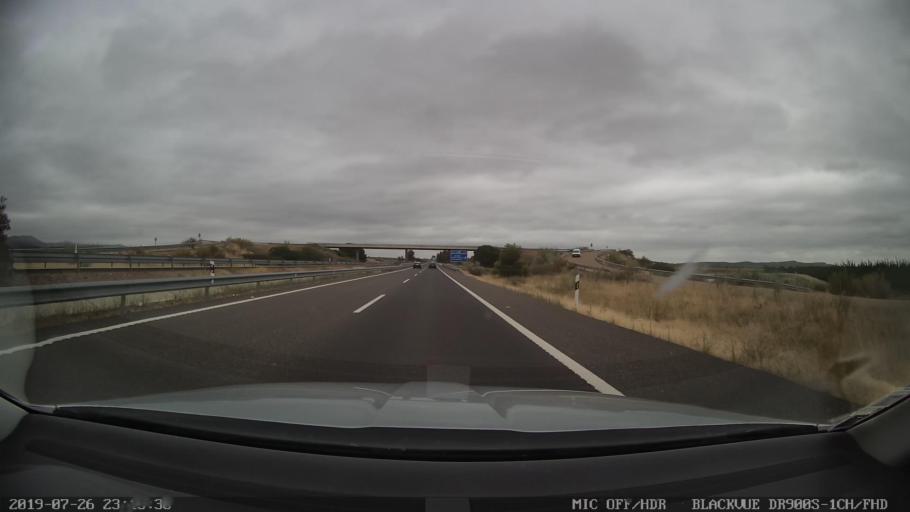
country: ES
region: Extremadura
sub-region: Provincia de Badajoz
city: Santa Amalia
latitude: 39.0241
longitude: -6.0786
